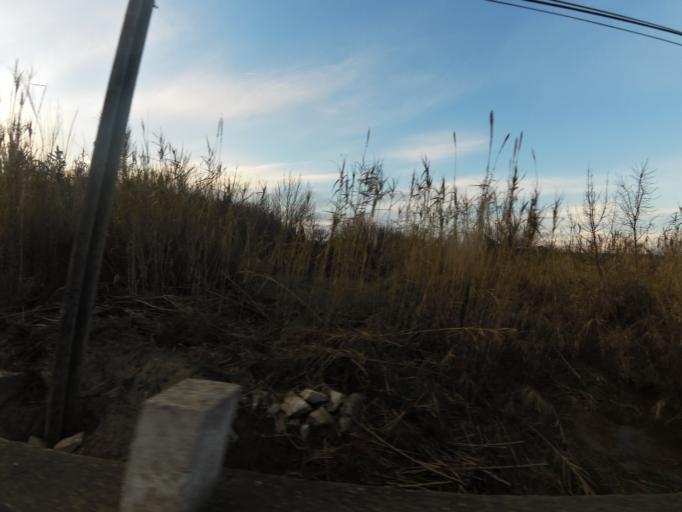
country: FR
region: Languedoc-Roussillon
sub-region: Departement du Gard
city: Clarensac
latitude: 43.8129
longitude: 4.1994
